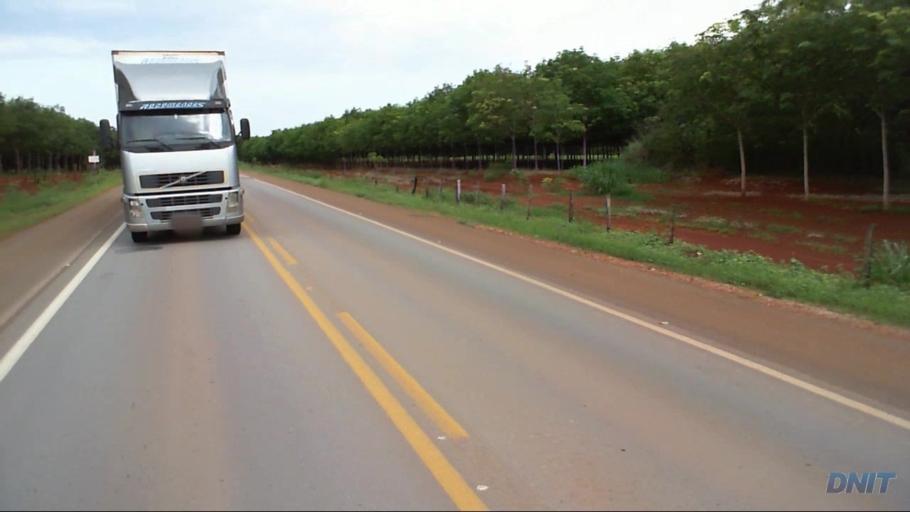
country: BR
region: Goias
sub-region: Barro Alto
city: Barro Alto
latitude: -14.8779
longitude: -48.9939
